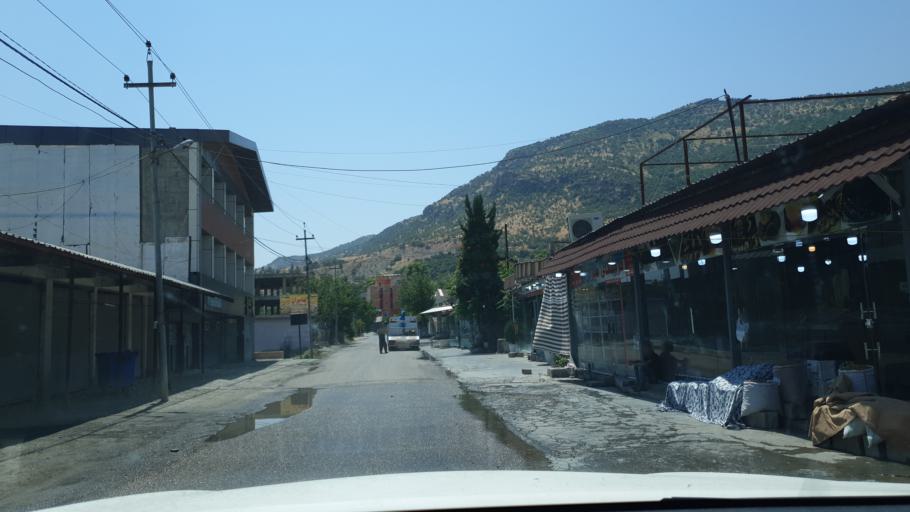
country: IQ
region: Arbil
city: Nahiyat Hiran
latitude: 36.2821
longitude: 44.4942
